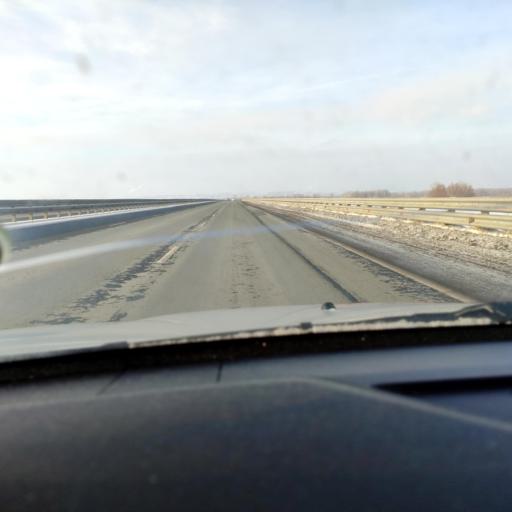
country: RU
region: Samara
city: Smyshlyayevka
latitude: 53.1567
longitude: 50.3393
